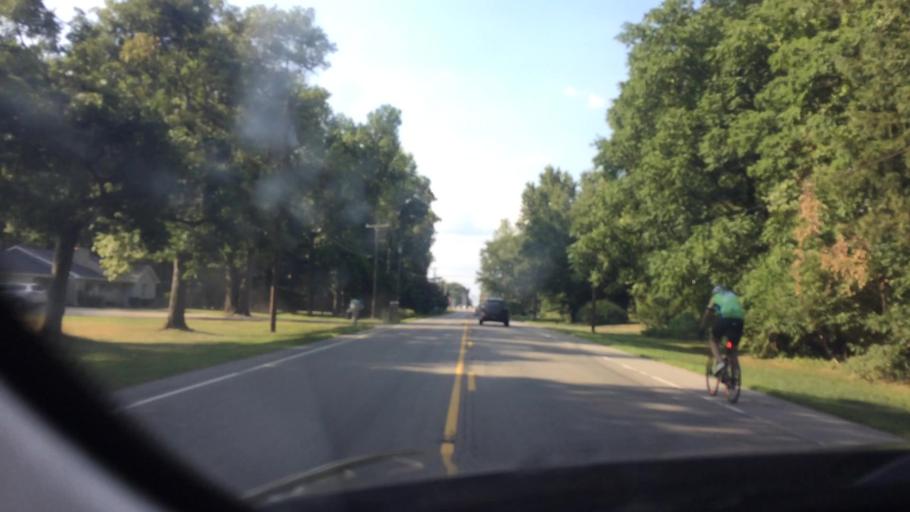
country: US
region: Ohio
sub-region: Lucas County
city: Holland
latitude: 41.6698
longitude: -83.7226
